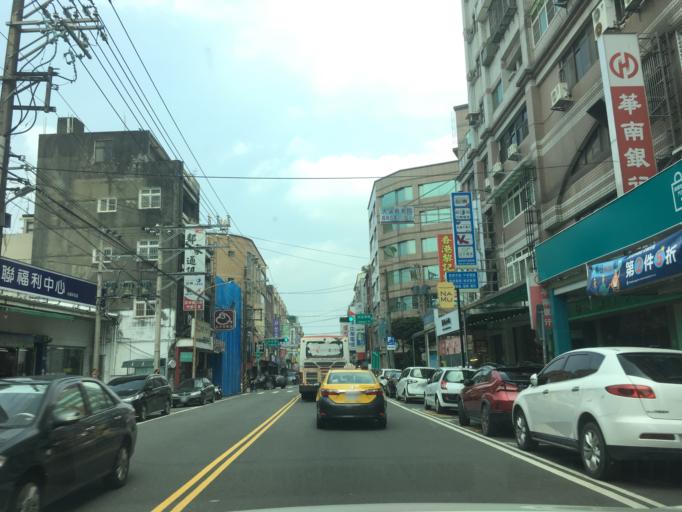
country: TW
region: Taiwan
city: Daxi
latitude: 24.8820
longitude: 121.2889
